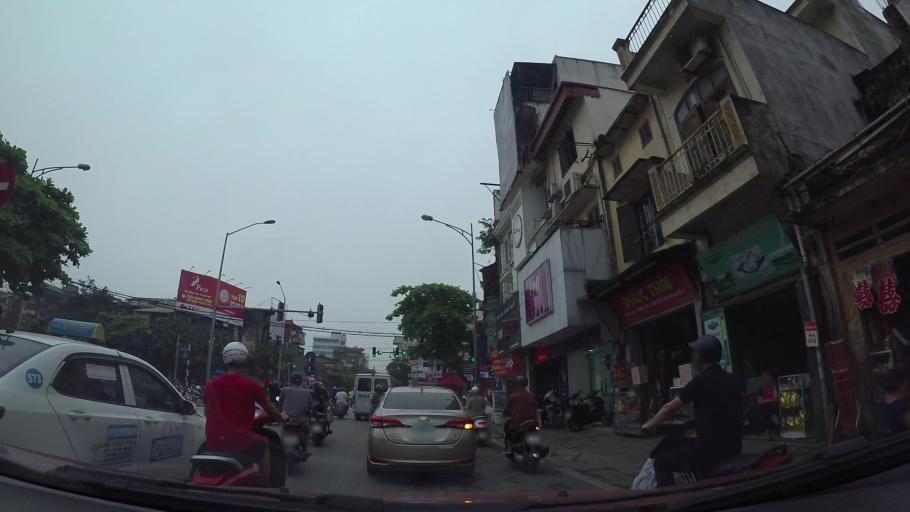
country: VN
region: Ha Noi
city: Hai BaTrung
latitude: 20.9963
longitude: 105.8499
